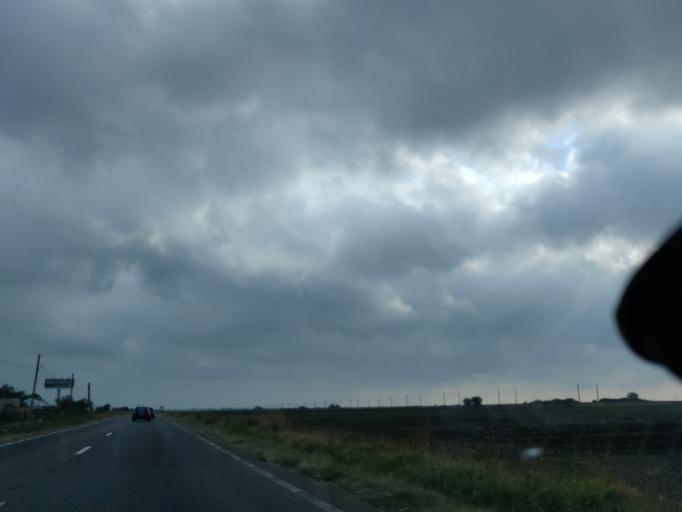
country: RO
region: Prahova
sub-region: Oras Mizil
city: Mizil
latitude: 45.0092
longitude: 26.4613
